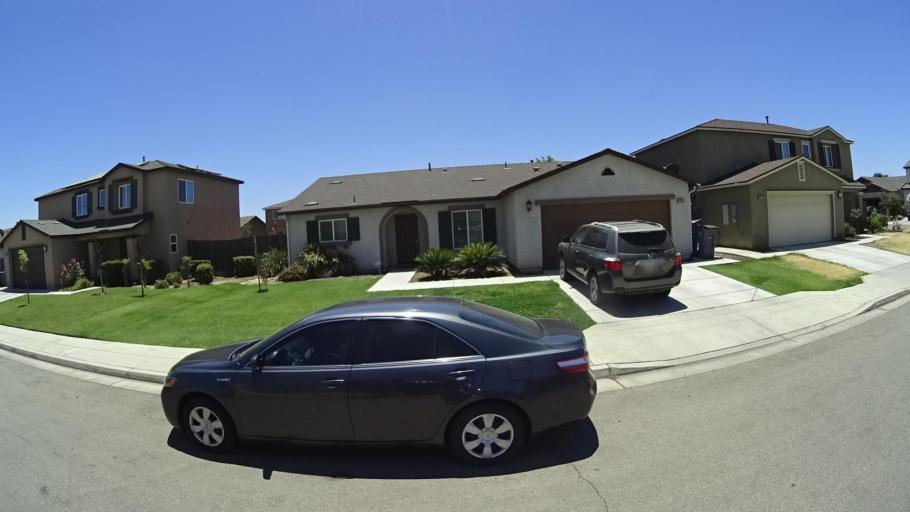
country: US
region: California
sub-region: Fresno County
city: Sunnyside
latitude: 36.7272
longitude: -119.6690
